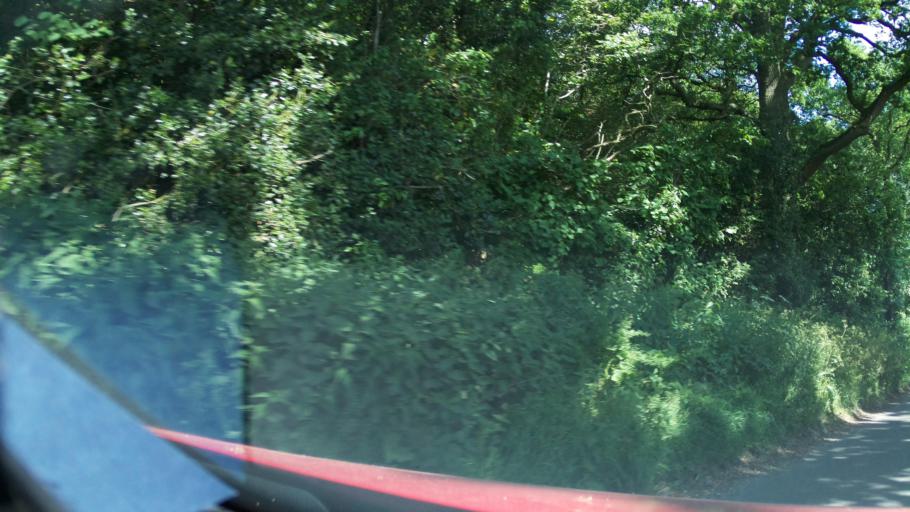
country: GB
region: England
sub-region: Wiltshire
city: Pewsey
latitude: 51.3467
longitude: -1.7873
